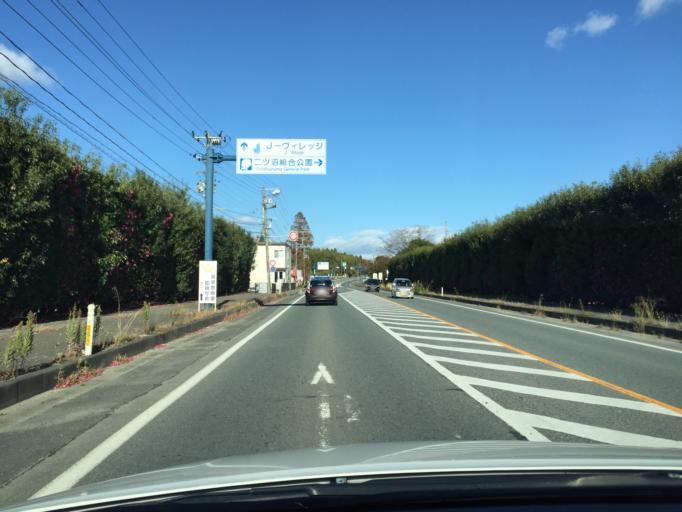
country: JP
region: Fukushima
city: Iwaki
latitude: 37.2307
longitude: 141.0002
